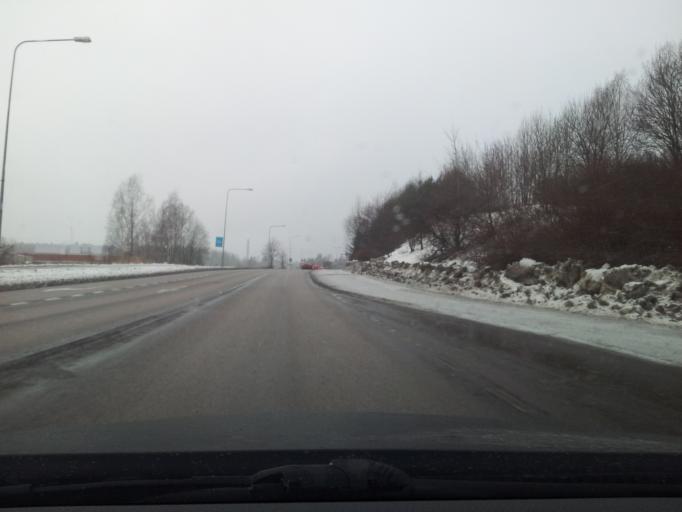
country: FI
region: Uusimaa
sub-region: Helsinki
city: Koukkuniemi
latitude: 60.1810
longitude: 24.7590
